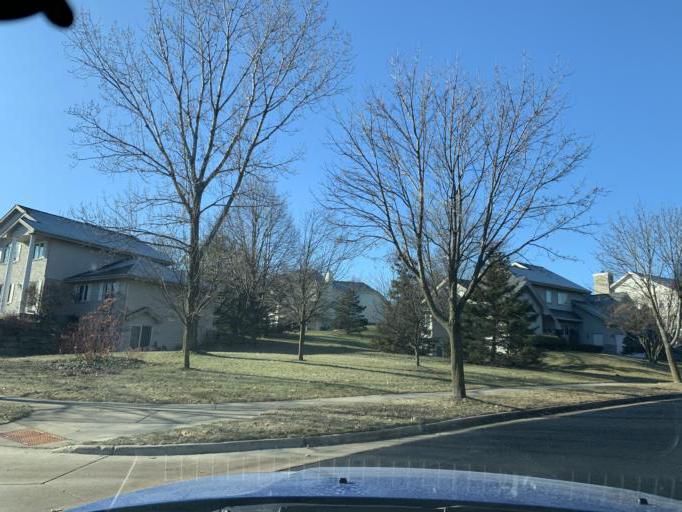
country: US
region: Wisconsin
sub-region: Dane County
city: Middleton
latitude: 43.0446
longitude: -89.5091
